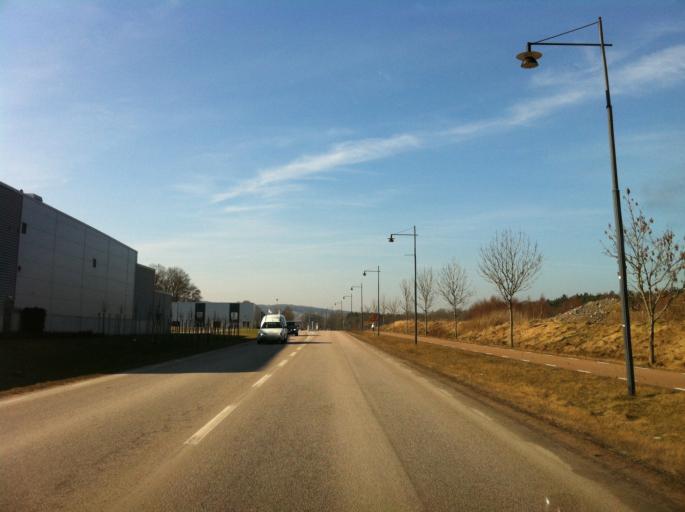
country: SE
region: Skane
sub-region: Bastads Kommun
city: Bastad
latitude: 56.4265
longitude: 12.8889
